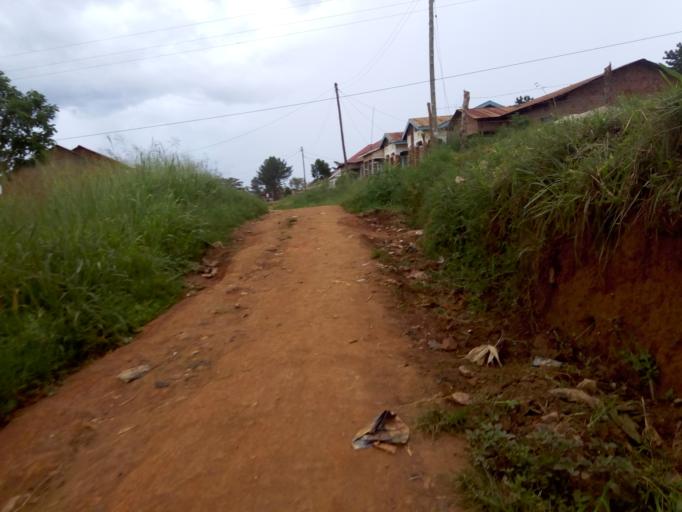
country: UG
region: Western Region
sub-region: Masindi District
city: Masindi
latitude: 1.6796
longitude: 31.7169
